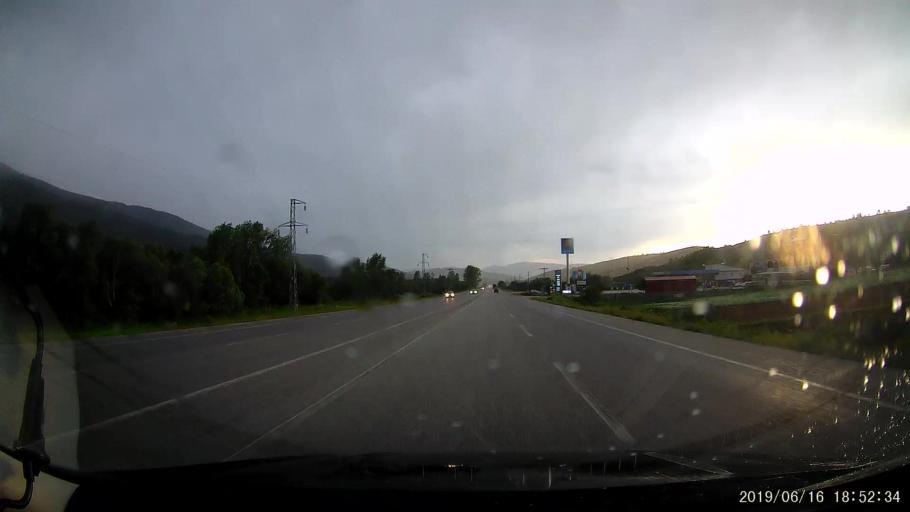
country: TR
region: Erzincan
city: Catalcam
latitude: 39.9021
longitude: 38.8983
